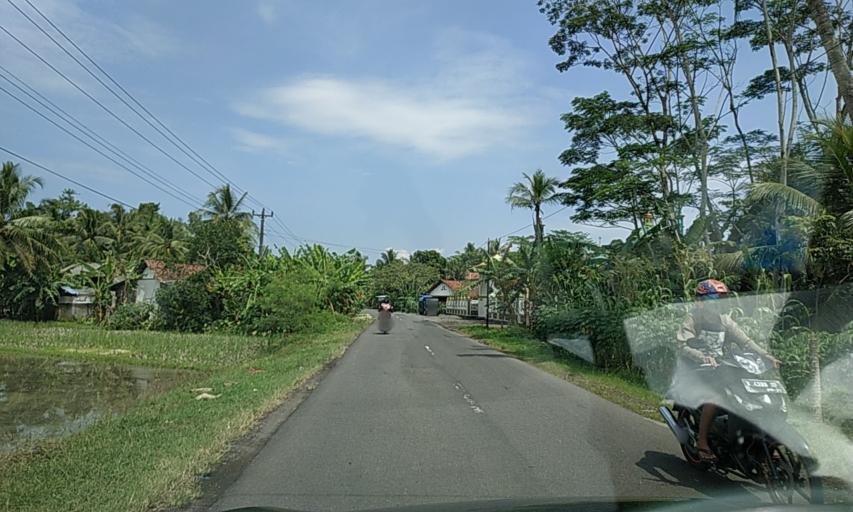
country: ID
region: Central Java
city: Kedungbulu
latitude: -7.5259
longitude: 108.7843
